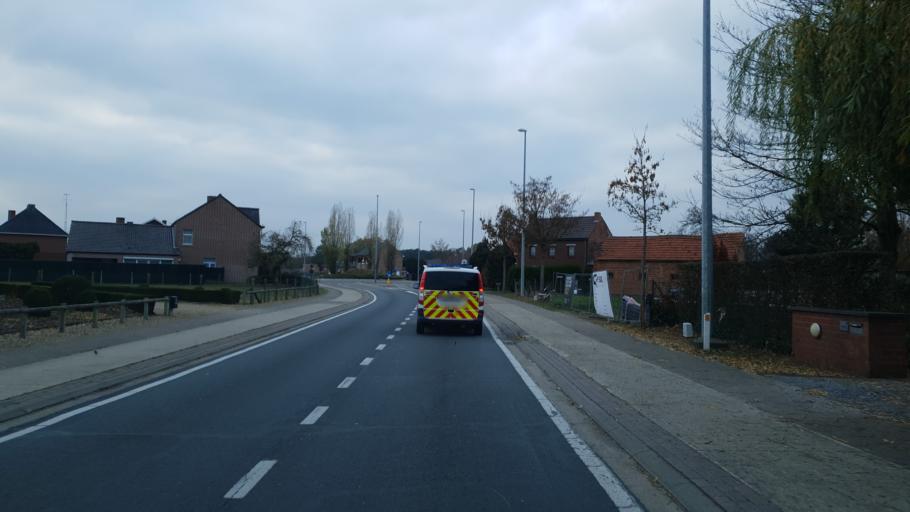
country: BE
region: Flanders
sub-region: Provincie Limburg
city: Zutendaal
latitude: 50.9317
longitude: 5.5914
